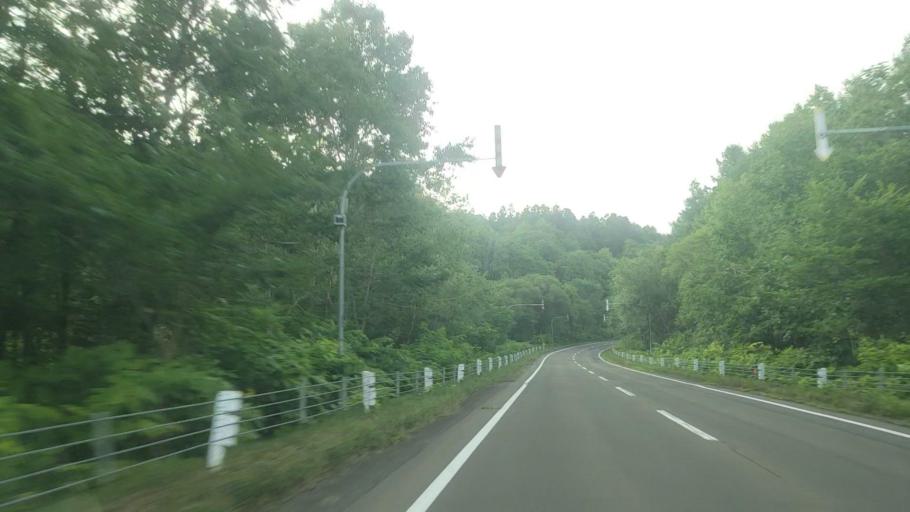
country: JP
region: Hokkaido
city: Bibai
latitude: 43.1147
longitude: 142.0992
